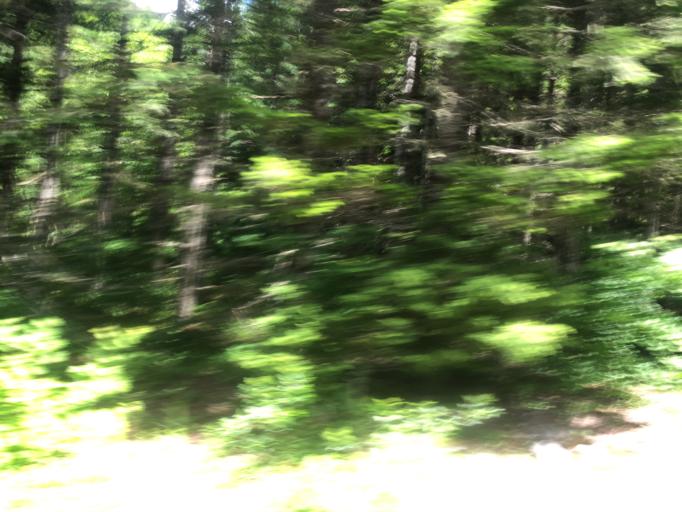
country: US
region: Oregon
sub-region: Clackamas County
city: Mount Hood Village
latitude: 45.4694
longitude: -121.8546
